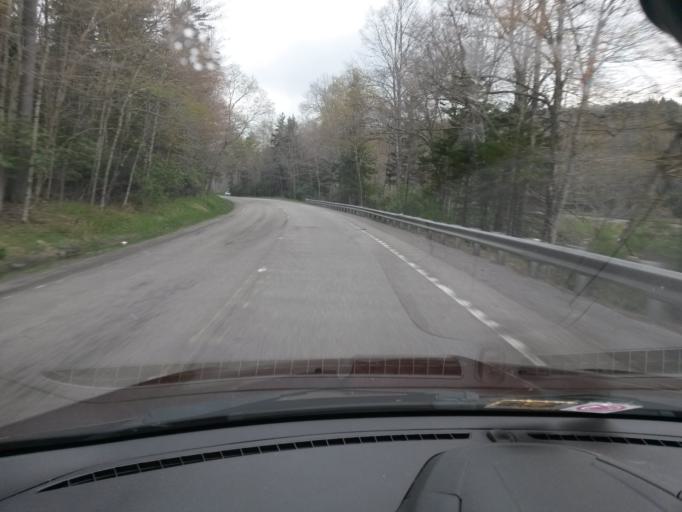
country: US
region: West Virginia
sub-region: Randolph County
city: Elkins
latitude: 38.6238
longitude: -79.8680
